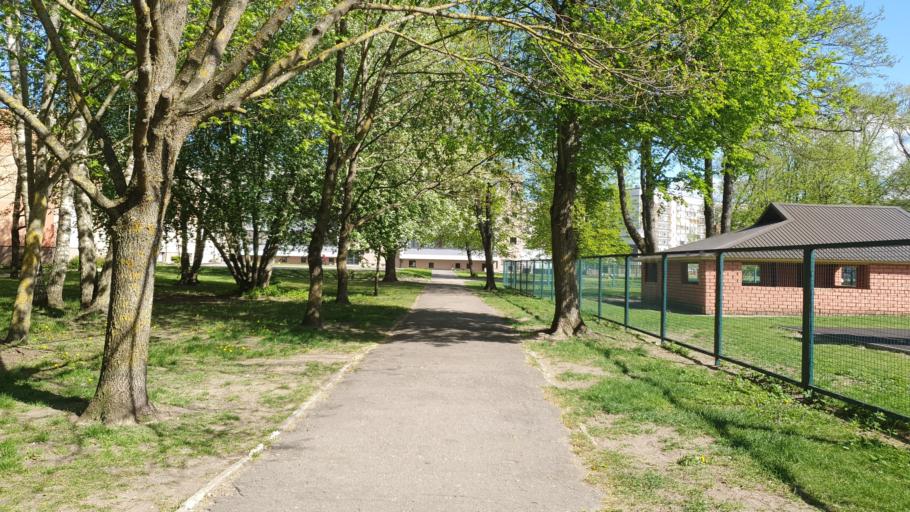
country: LV
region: Marupe
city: Marupe
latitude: 56.9460
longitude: 24.0046
